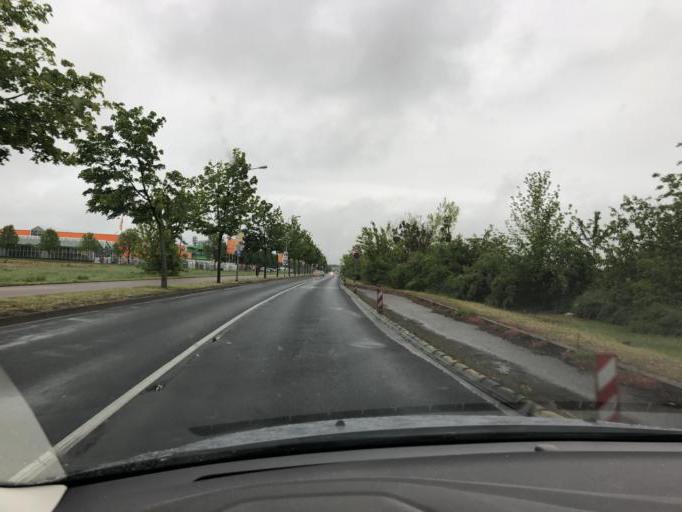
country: DE
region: Saxony-Anhalt
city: Dessau
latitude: 51.8215
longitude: 12.2157
